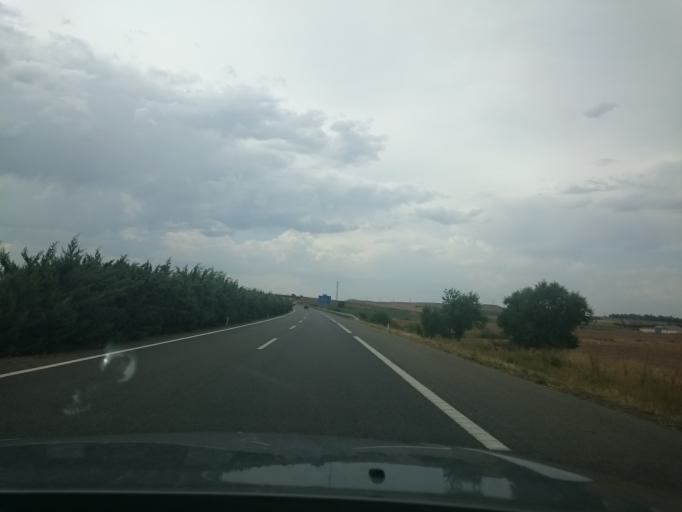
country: ES
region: Navarre
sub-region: Provincia de Navarra
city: Fontellas
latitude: 42.0053
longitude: -1.5868
